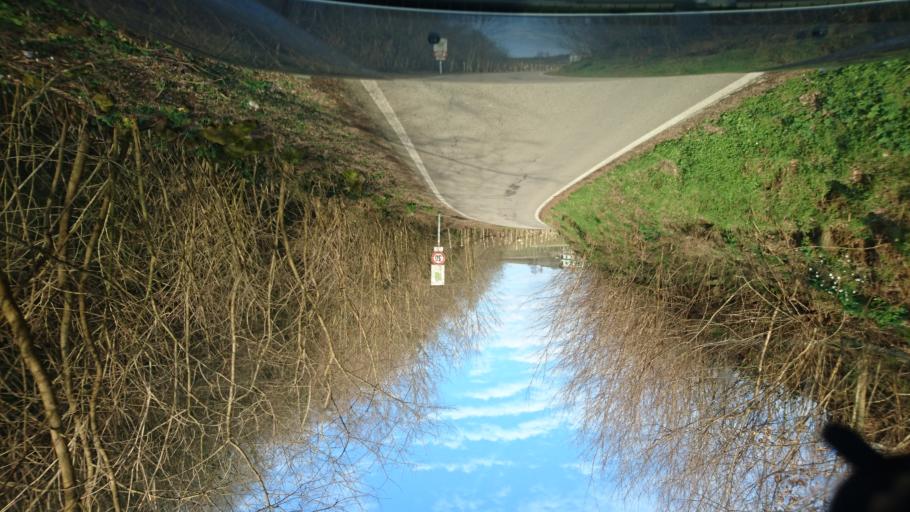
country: IT
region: Veneto
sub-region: Provincia di Padova
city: Vo
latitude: 45.3425
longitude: 11.6619
